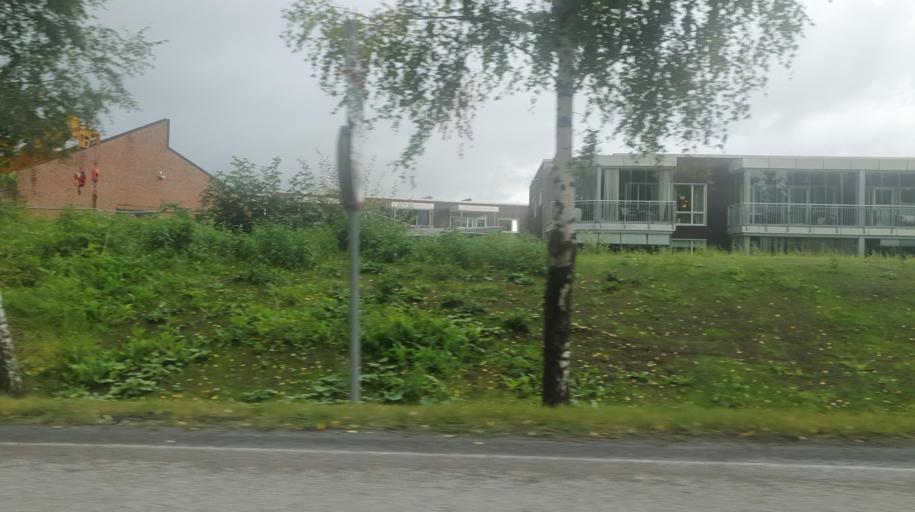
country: NO
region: Nord-Trondelag
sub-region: Verdal
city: Verdal
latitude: 63.7919
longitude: 11.4895
